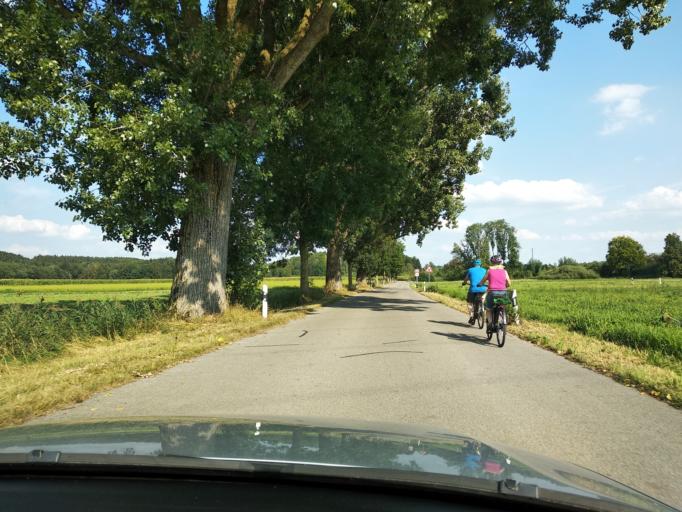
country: DE
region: Bavaria
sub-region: Swabia
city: Memmingen
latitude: 48.0046
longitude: 10.1899
